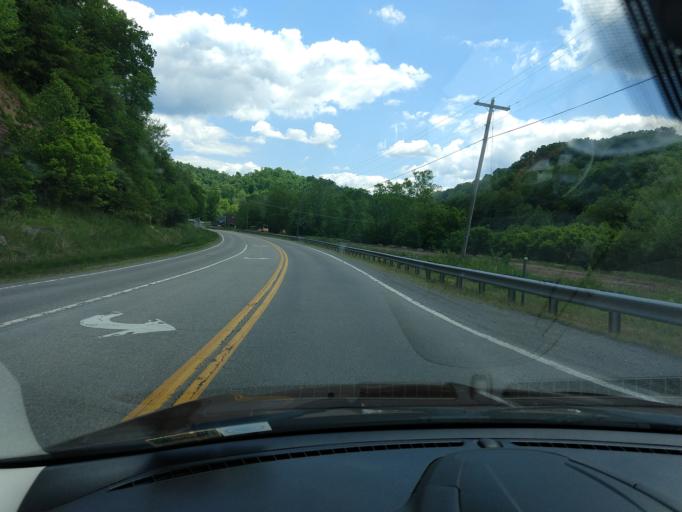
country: US
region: West Virginia
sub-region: Gilmer County
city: Glenville
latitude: 38.9297
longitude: -80.7844
